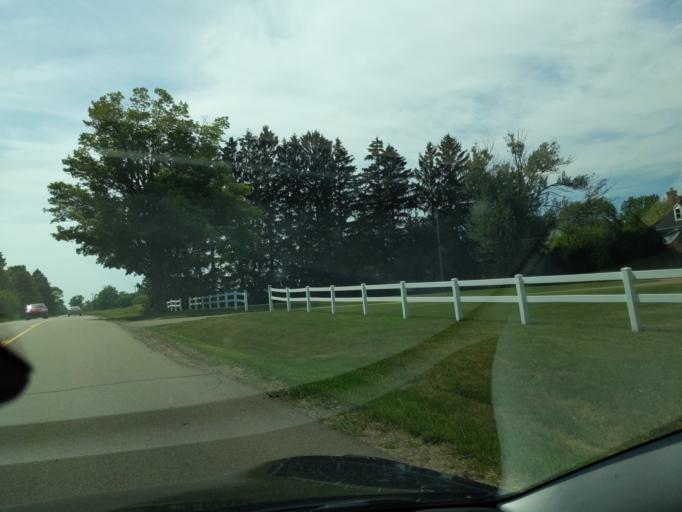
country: US
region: Michigan
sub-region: Eaton County
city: Grand Ledge
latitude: 42.7119
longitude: -84.7664
